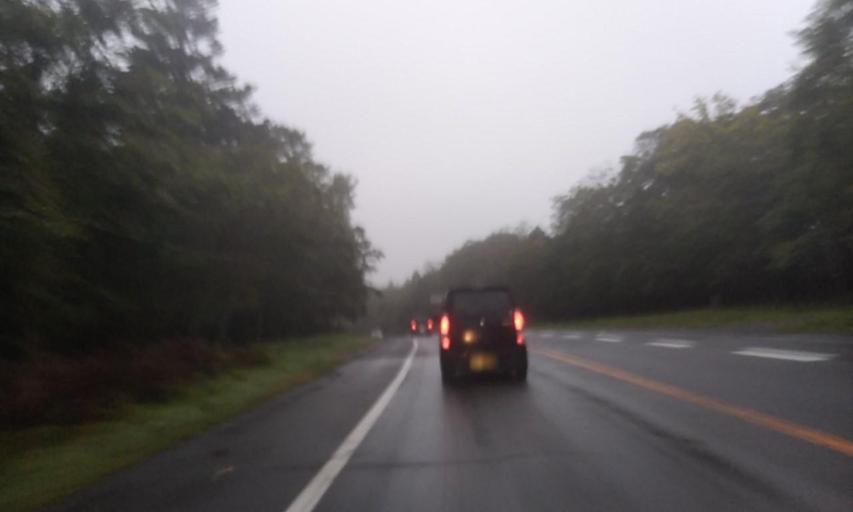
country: JP
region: Hokkaido
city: Kushiro
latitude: 42.9916
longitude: 144.5207
